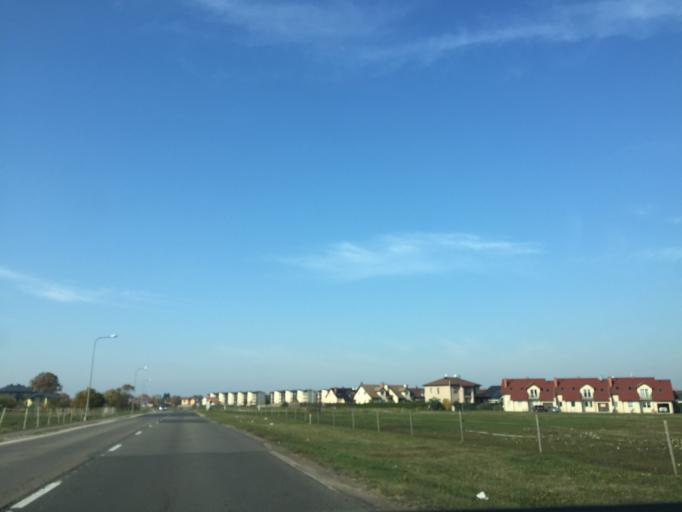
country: LV
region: Marupe
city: Marupe
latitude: 56.8889
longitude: 24.0601
